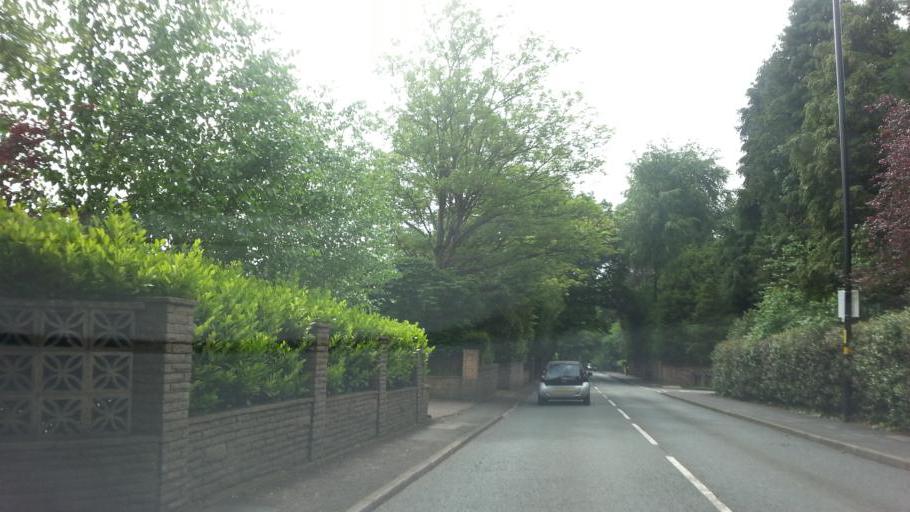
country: GB
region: England
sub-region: City and Borough of Birmingham
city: Sutton Coldfield
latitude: 52.5813
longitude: -1.8320
